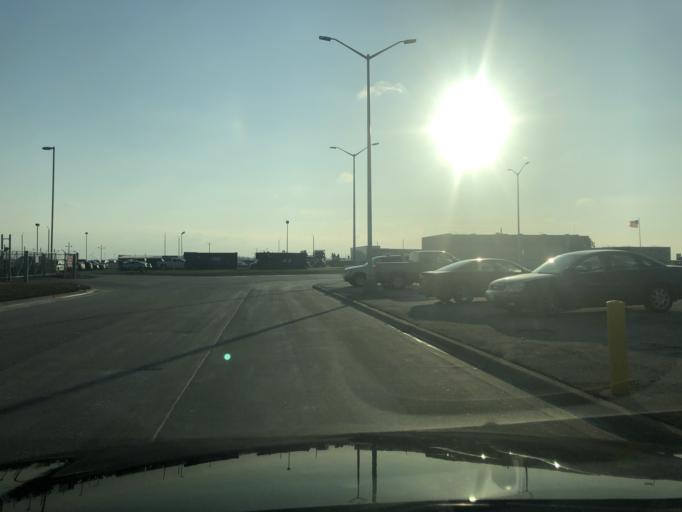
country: US
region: Michigan
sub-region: Wayne County
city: Romulus
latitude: 42.2350
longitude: -83.3422
